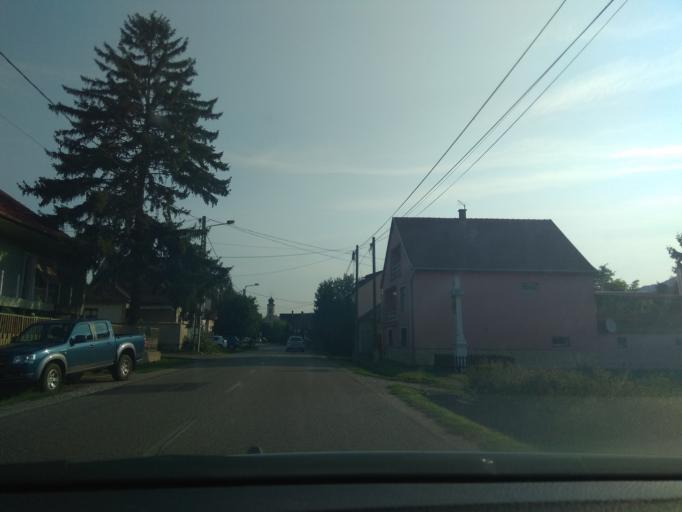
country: HU
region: Heves
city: Felsotarkany
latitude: 47.9691
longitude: 20.4101
